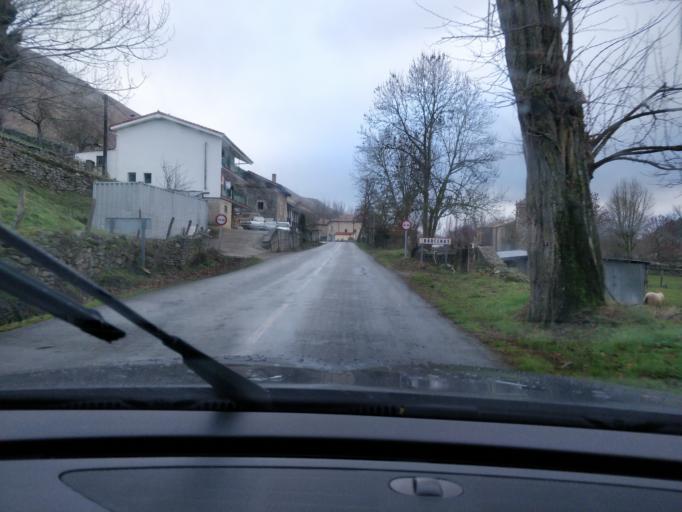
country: ES
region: Castille and Leon
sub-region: Provincia de Burgos
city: Espinosa de los Monteros
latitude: 43.0988
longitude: -3.5674
